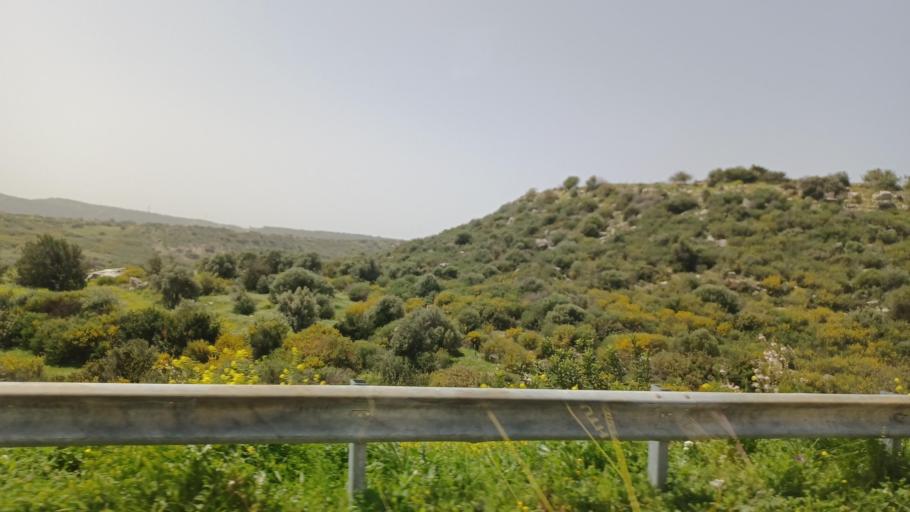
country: CY
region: Limassol
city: Pissouri
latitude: 34.7231
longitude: 32.7368
